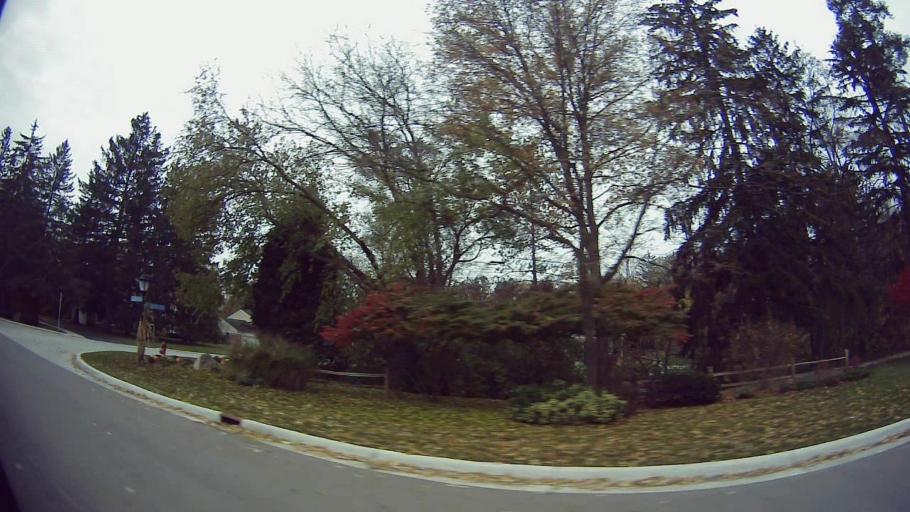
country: US
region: Michigan
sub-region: Oakland County
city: Bingham Farms
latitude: 42.5194
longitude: -83.2630
